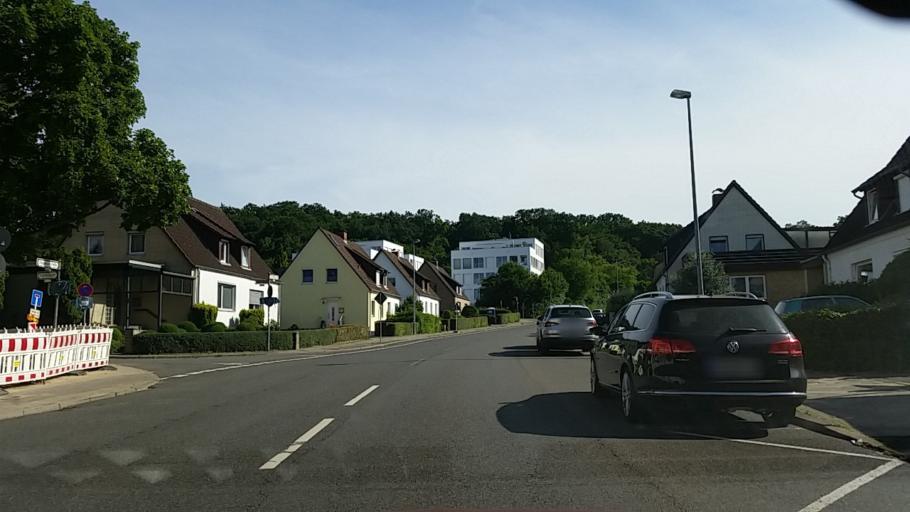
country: DE
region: Lower Saxony
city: Wolfsburg
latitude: 52.4197
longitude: 10.7618
